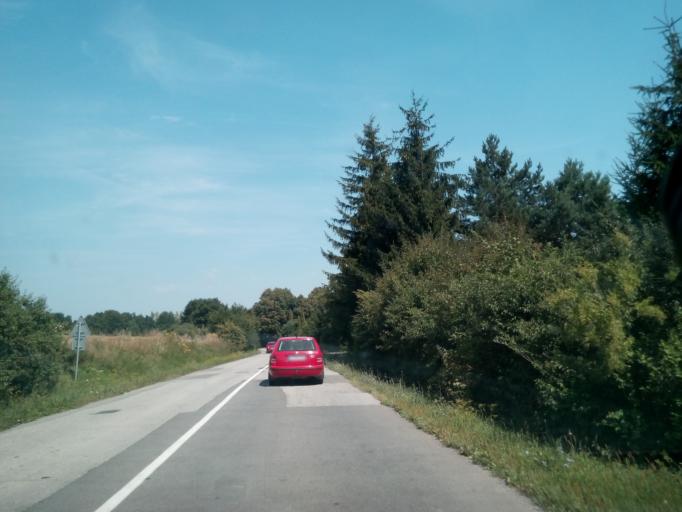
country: SK
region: Kosicky
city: Kosice
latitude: 48.7846
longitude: 21.2431
